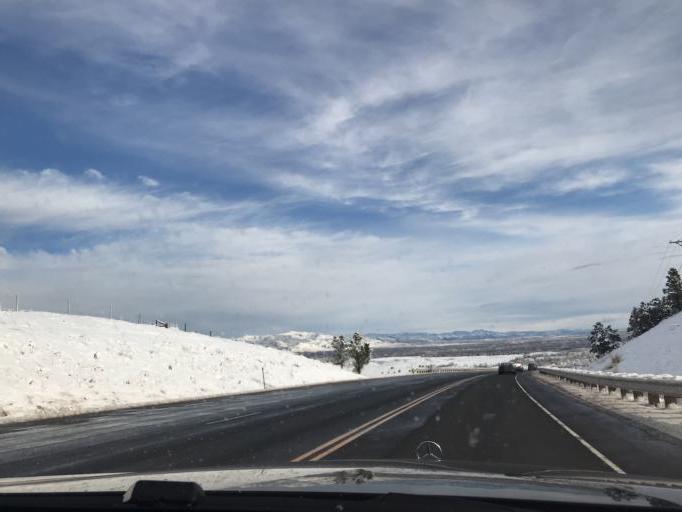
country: US
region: Colorado
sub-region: Boulder County
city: Superior
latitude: 39.9349
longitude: -105.2366
